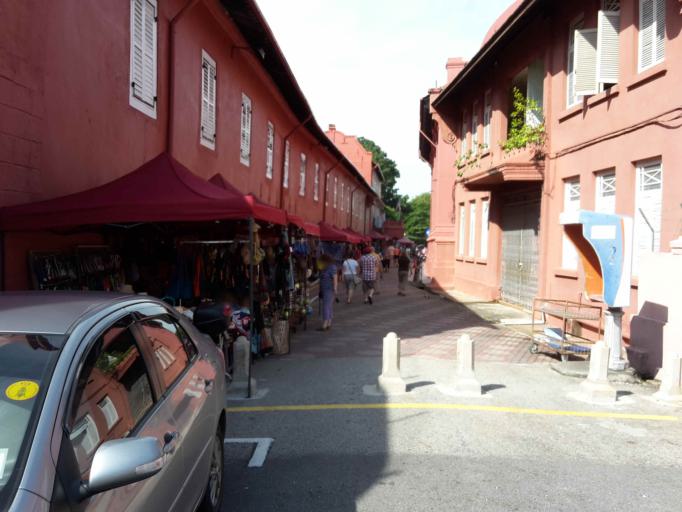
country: MY
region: Melaka
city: Malacca
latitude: 2.1943
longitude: 102.2500
